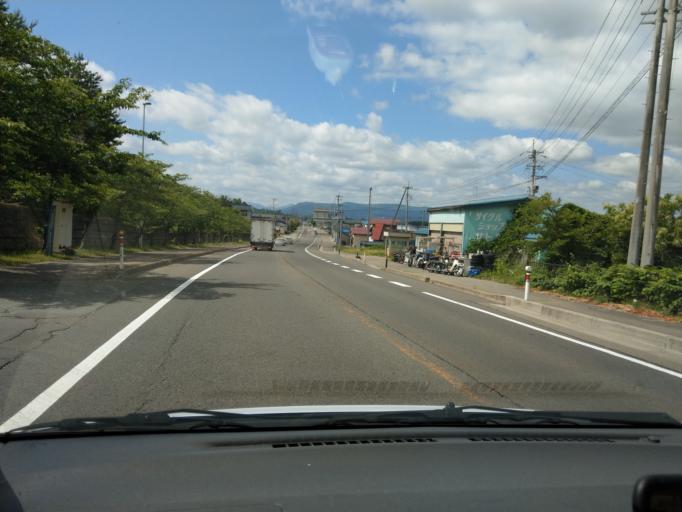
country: JP
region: Akita
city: Yuzawa
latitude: 39.2007
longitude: 140.5060
